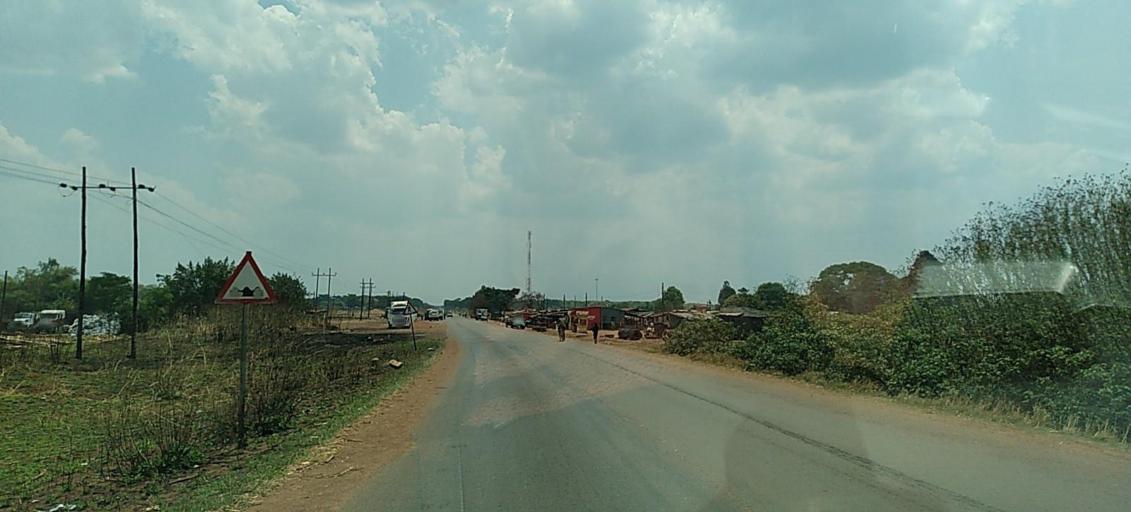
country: ZM
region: Copperbelt
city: Kalulushi
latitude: -12.8341
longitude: 27.9701
